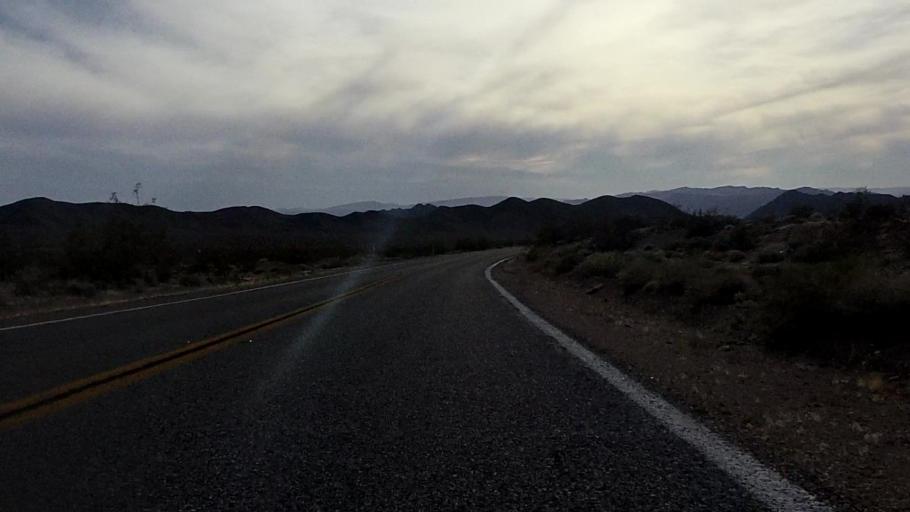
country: US
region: Nevada
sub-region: Nye County
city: Pahrump
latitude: 35.9139
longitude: -116.4432
